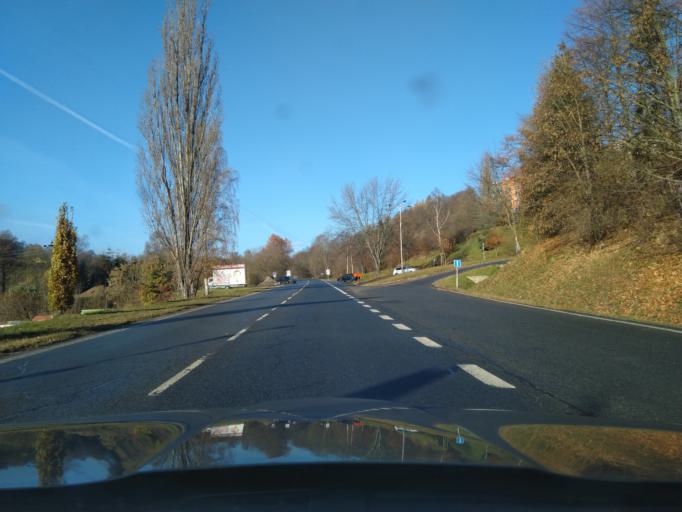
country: CZ
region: Jihocesky
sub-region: Okres Prachatice
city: Vimperk
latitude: 49.0599
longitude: 13.7747
